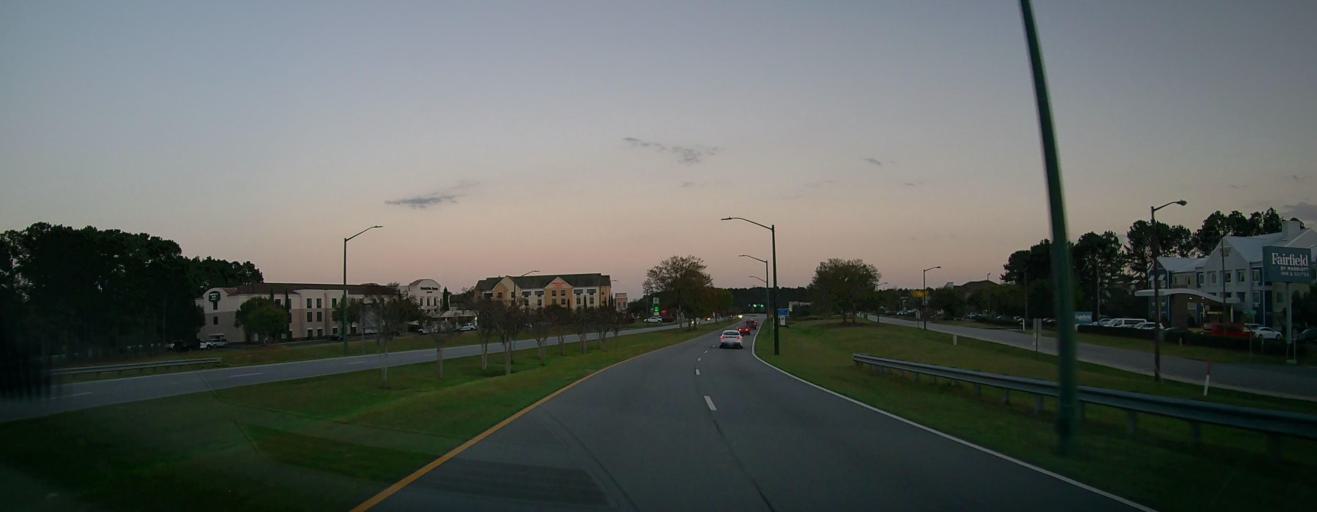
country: US
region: Georgia
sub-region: Chatham County
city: Pooler
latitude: 32.1407
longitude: -81.2369
